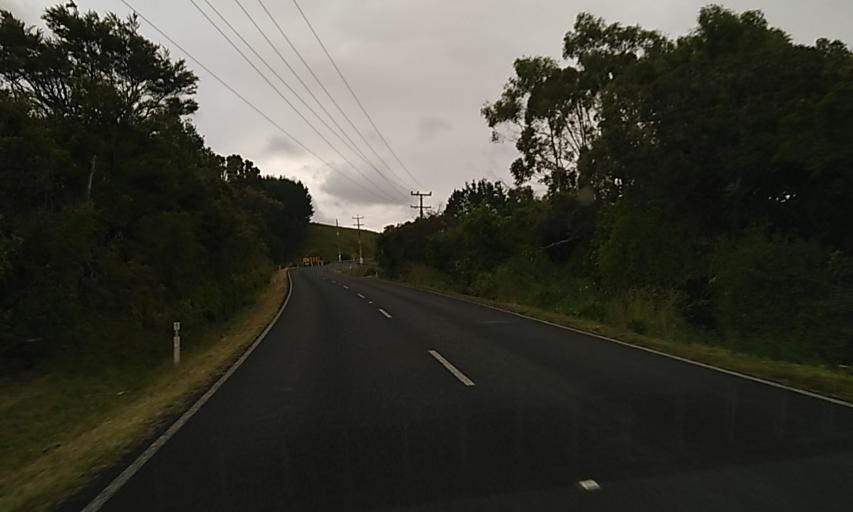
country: NZ
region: Auckland
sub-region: Auckland
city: Pukekohe East
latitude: -37.3173
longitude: 174.9369
